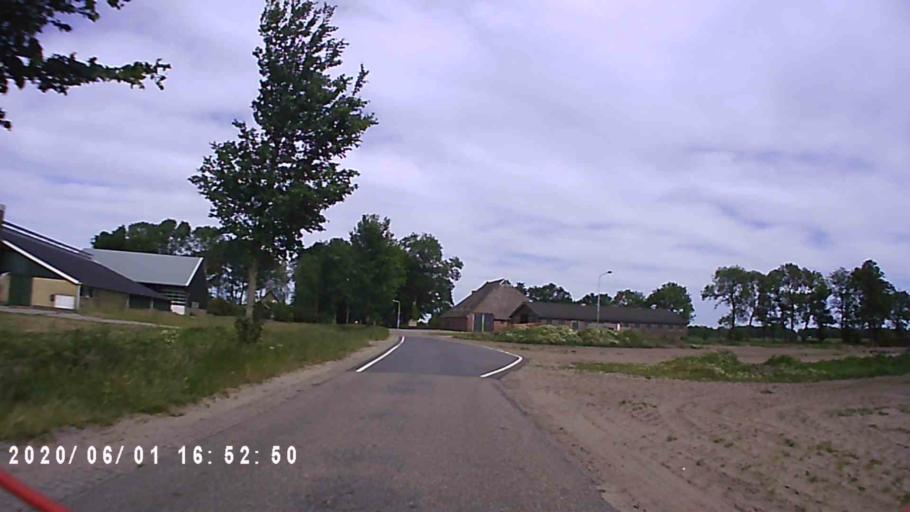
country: NL
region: Friesland
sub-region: Gemeente Tytsjerksteradiel
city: Tytsjerk
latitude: 53.1892
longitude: 5.9181
